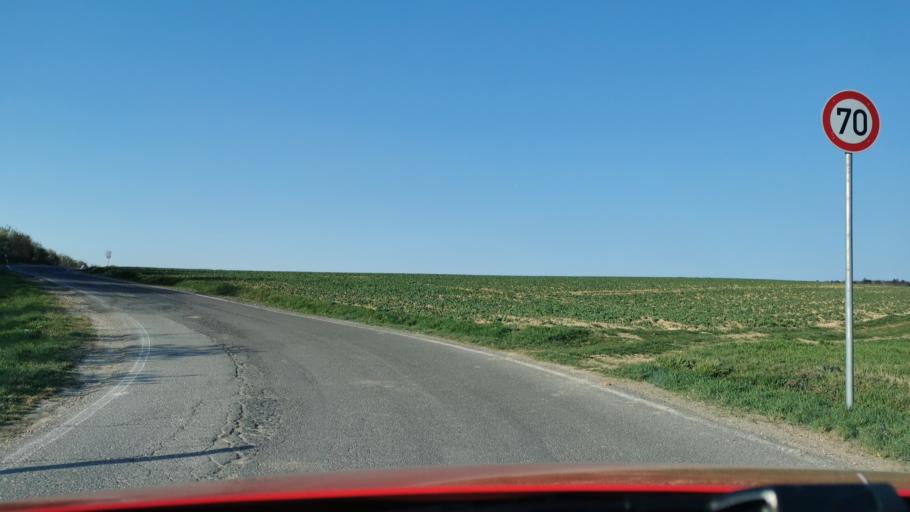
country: DE
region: Rheinland-Pfalz
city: Newel
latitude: 49.7998
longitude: 6.5467
